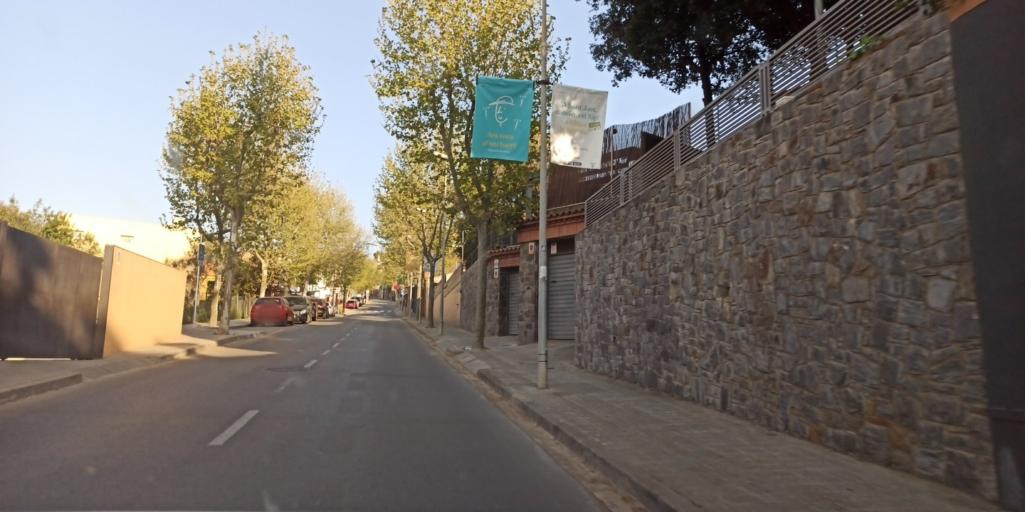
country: ES
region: Catalonia
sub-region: Provincia de Barcelona
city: Sant Just Desvern
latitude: 41.3877
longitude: 2.0768
